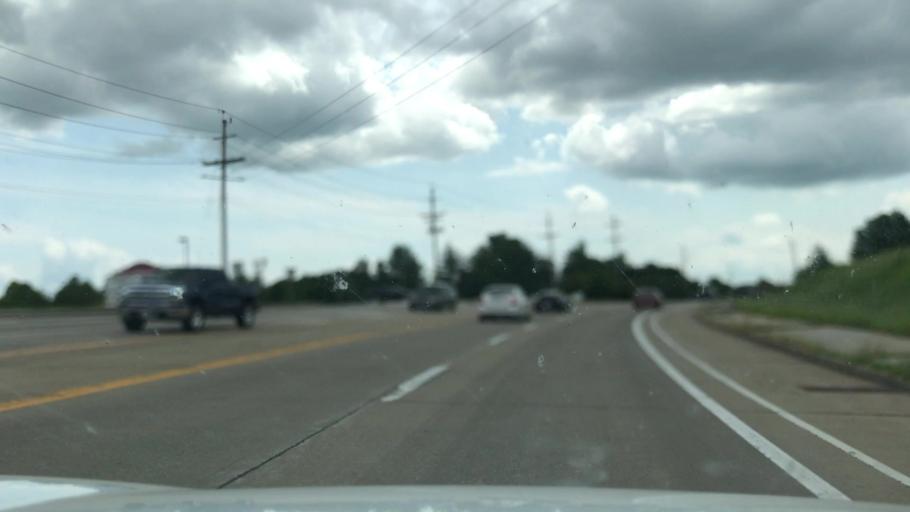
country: US
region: Missouri
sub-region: Saint Charles County
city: Weldon Spring
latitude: 38.7339
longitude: -90.6915
